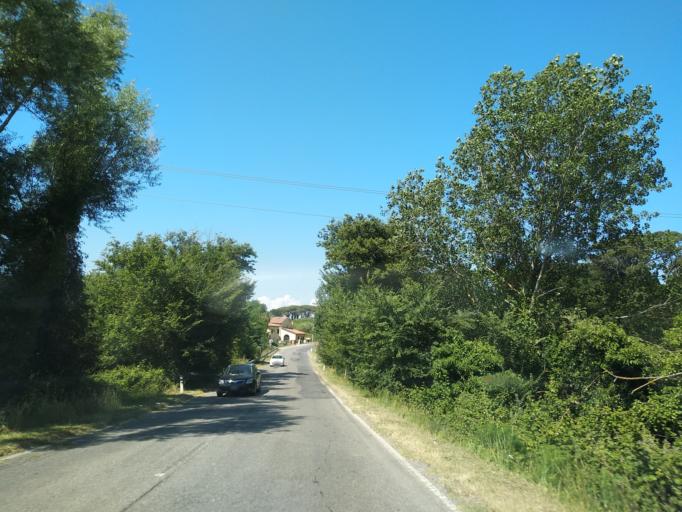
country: IT
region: Tuscany
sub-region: Provincia di Livorno
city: Livorno
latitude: 43.5664
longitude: 10.3606
